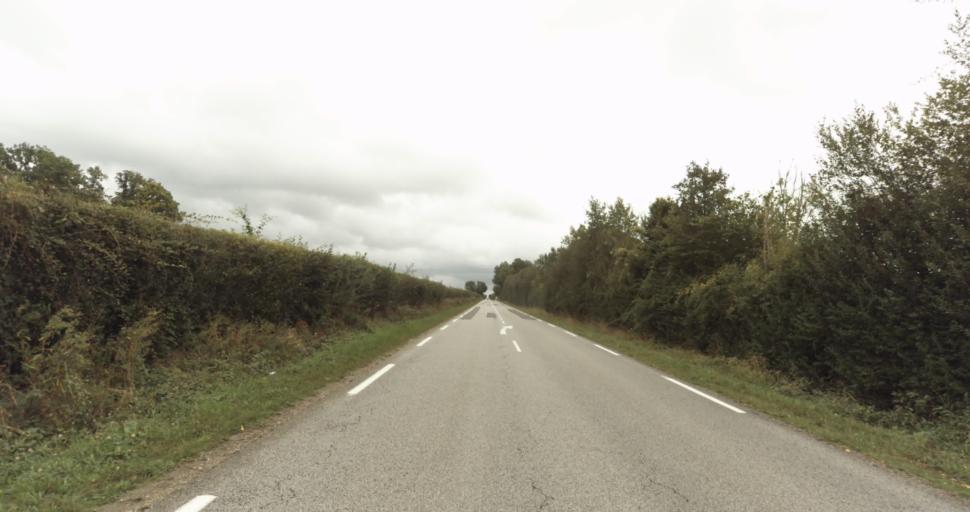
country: FR
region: Lower Normandy
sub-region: Departement de l'Orne
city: Sainte-Gauburge-Sainte-Colombe
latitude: 48.7082
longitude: 0.4357
